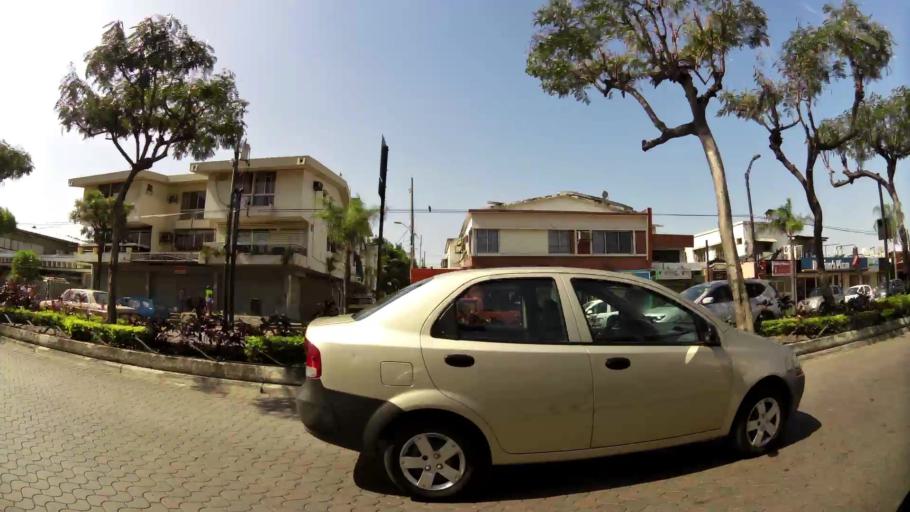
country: EC
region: Guayas
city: Guayaquil
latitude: -2.1709
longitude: -79.9089
